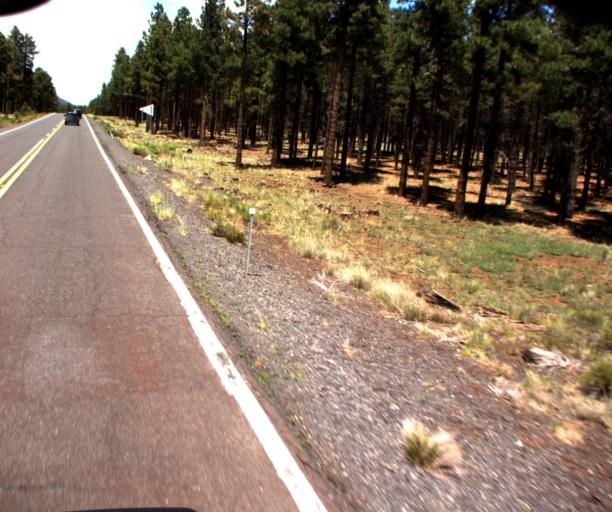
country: US
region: Arizona
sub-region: Coconino County
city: Parks
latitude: 35.4536
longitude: -111.7745
